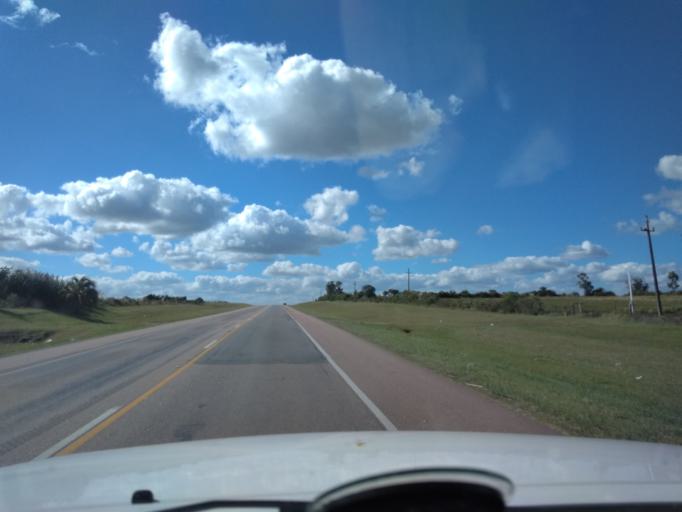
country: UY
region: Canelones
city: Canelones
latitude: -34.4905
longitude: -56.2819
